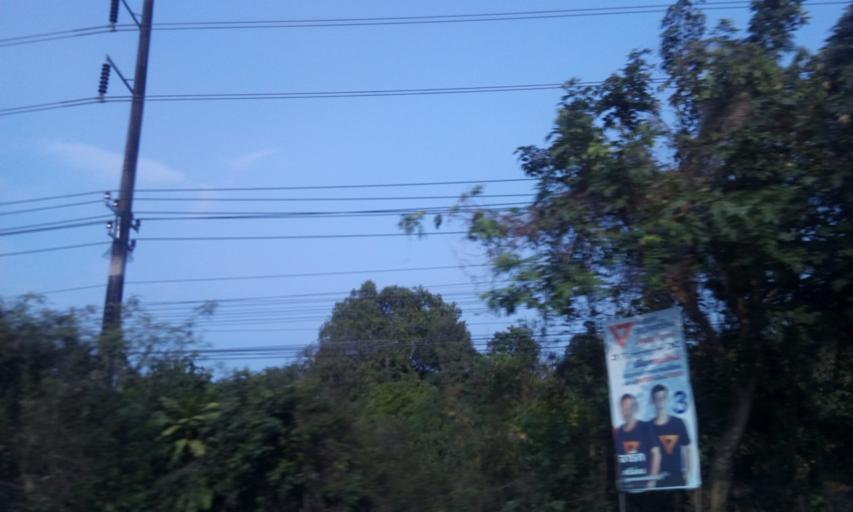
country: TH
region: Chanthaburi
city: Tha Mai
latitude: 12.6685
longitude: 102.0072
